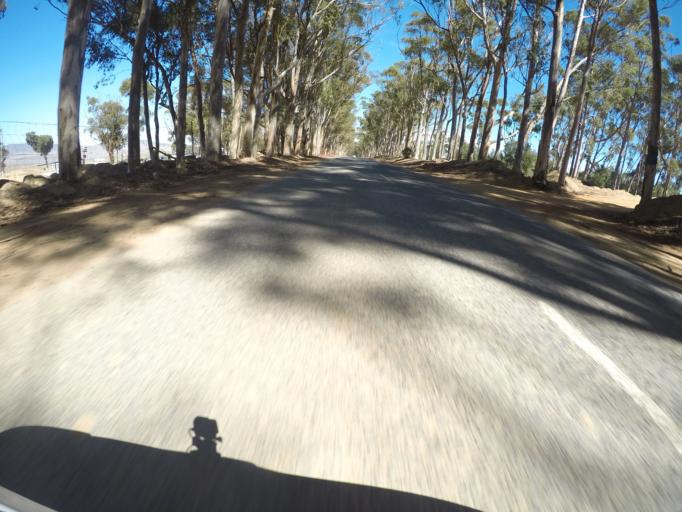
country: ZA
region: Western Cape
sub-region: City of Cape Town
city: Sunset Beach
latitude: -33.7615
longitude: 18.5525
